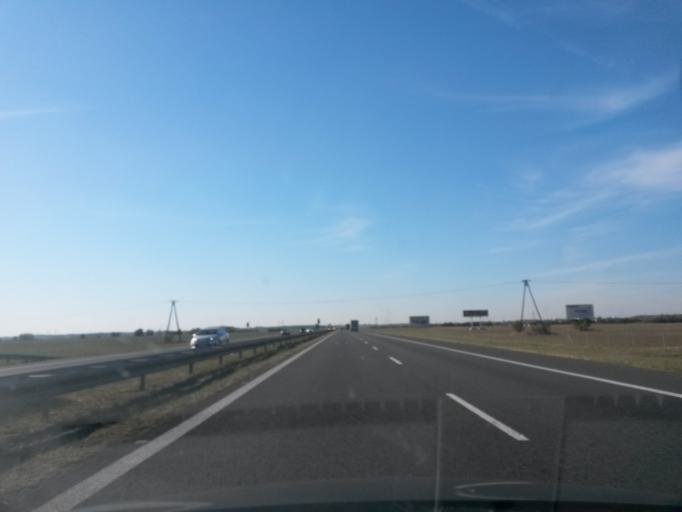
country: PL
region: Opole Voivodeship
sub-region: Powiat brzeski
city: Lewin Brzeski
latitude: 50.7114
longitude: 17.5900
